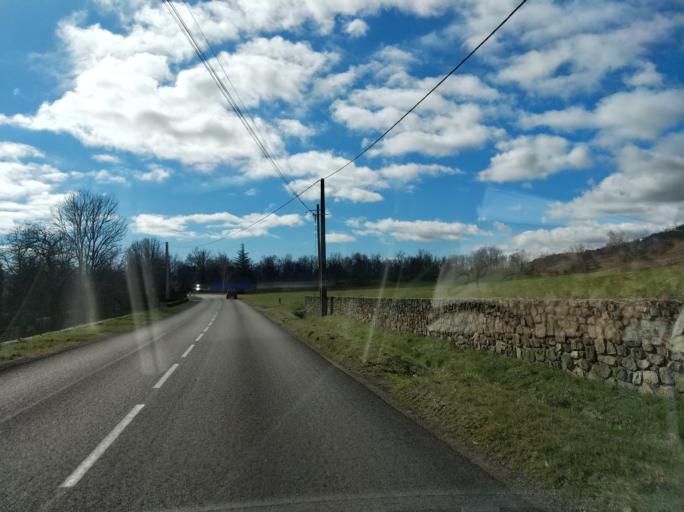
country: FR
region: Rhone-Alpes
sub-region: Departement de la Loire
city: Pelussin
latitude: 45.3962
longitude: 4.6863
